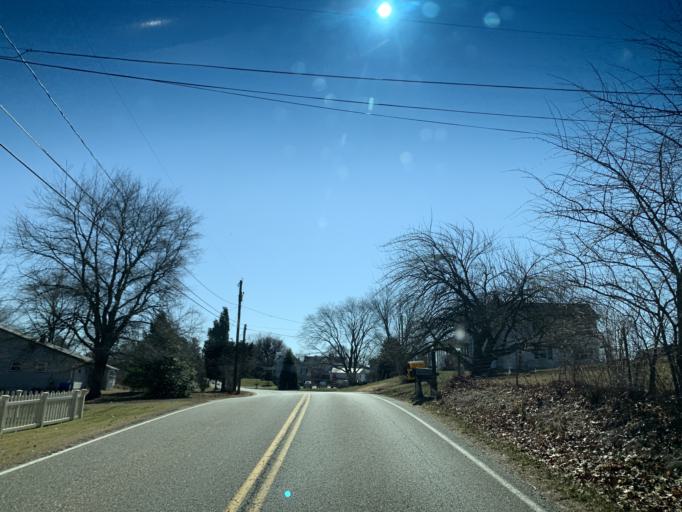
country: US
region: Maryland
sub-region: Cecil County
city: Perryville
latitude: 39.6040
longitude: -76.0729
